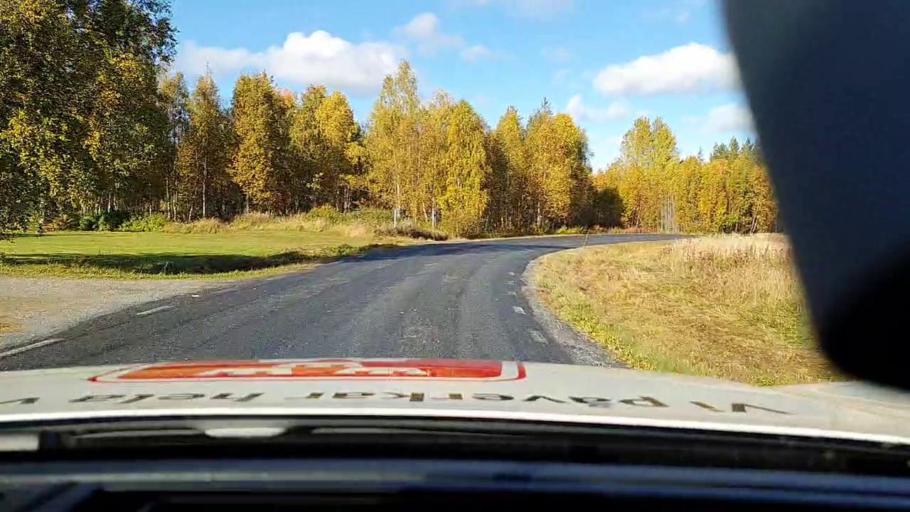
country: SE
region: Vaesterbotten
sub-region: Skelleftea Kommun
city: Langsele
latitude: 65.0061
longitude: 20.0887
